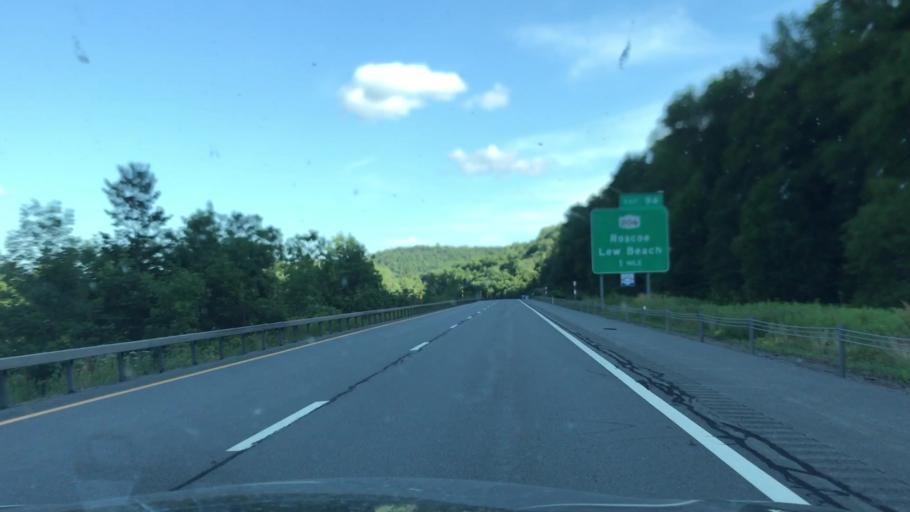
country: US
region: New York
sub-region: Sullivan County
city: Livingston Manor
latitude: 41.9430
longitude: -74.9304
